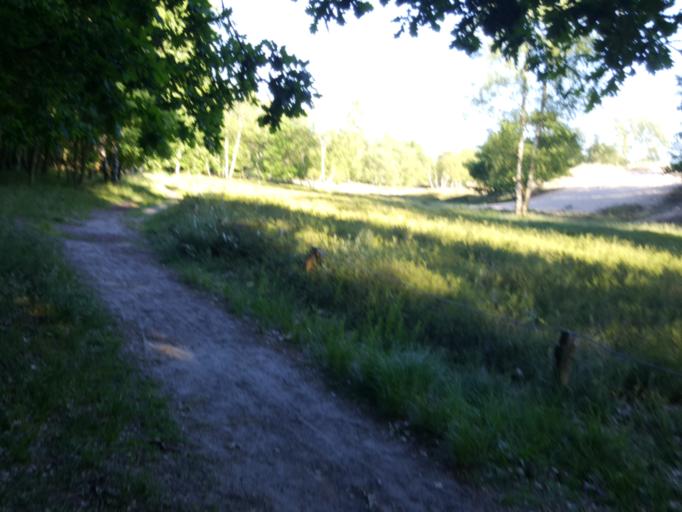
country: DE
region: Schleswig-Holstein
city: Oststeinbek
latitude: 53.5104
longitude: 10.1580
